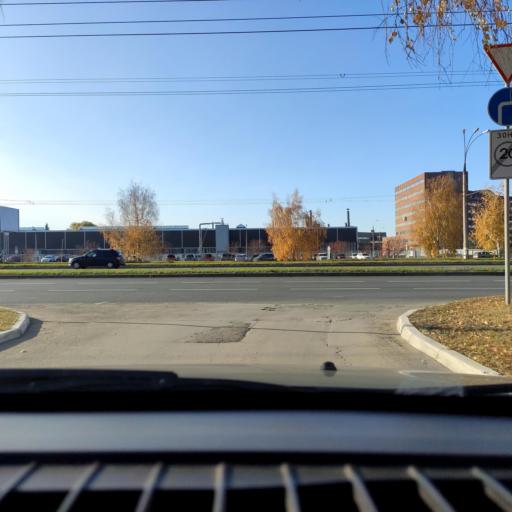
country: RU
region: Samara
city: Tol'yatti
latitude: 53.5492
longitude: 49.2667
